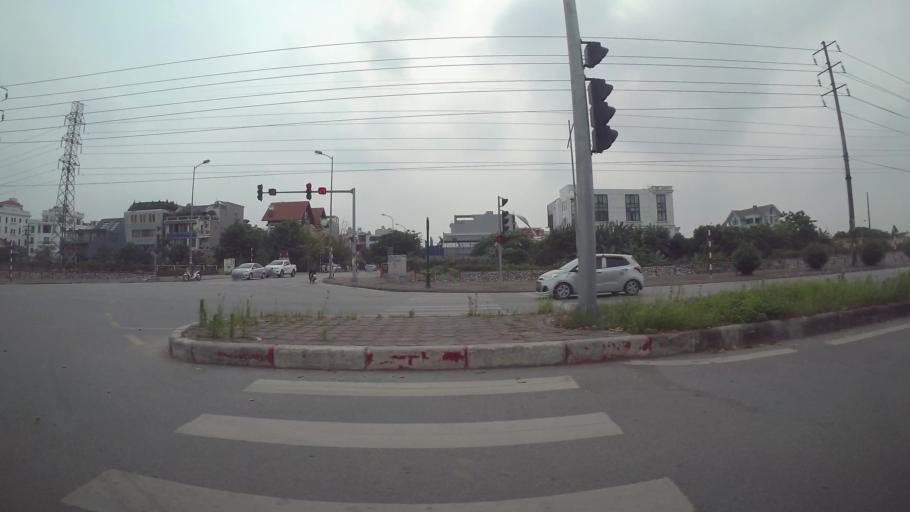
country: VN
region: Ha Noi
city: Trau Quy
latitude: 21.0555
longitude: 105.9054
